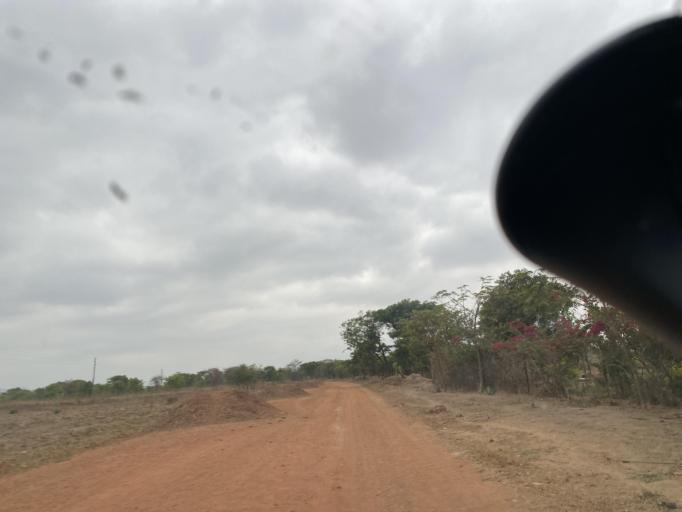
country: ZM
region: Lusaka
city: Chongwe
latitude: -15.2236
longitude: 28.7489
